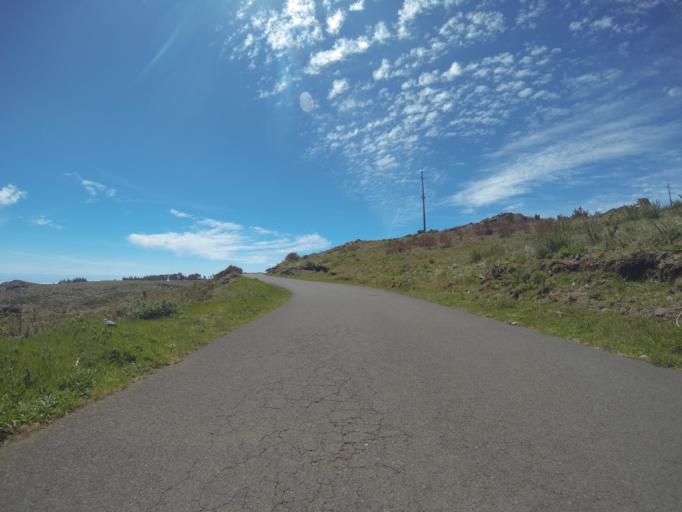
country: PT
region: Madeira
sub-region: Funchal
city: Nossa Senhora do Monte
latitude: 32.7167
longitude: -16.9122
